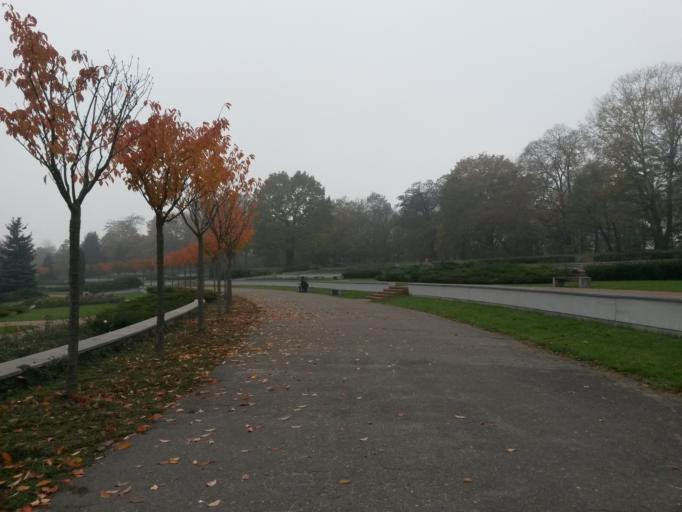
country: PL
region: Greater Poland Voivodeship
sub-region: Poznan
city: Poznan
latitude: 52.4245
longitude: 16.9322
